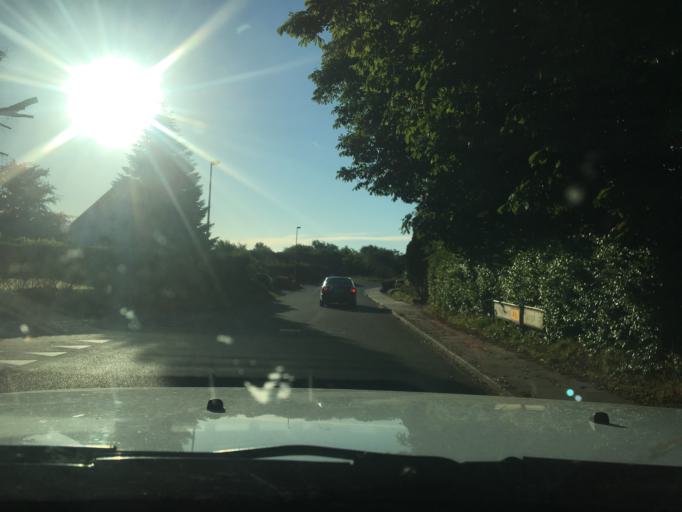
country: DK
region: Central Jutland
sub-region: Randers Kommune
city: Langa
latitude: 56.3941
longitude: 9.9565
